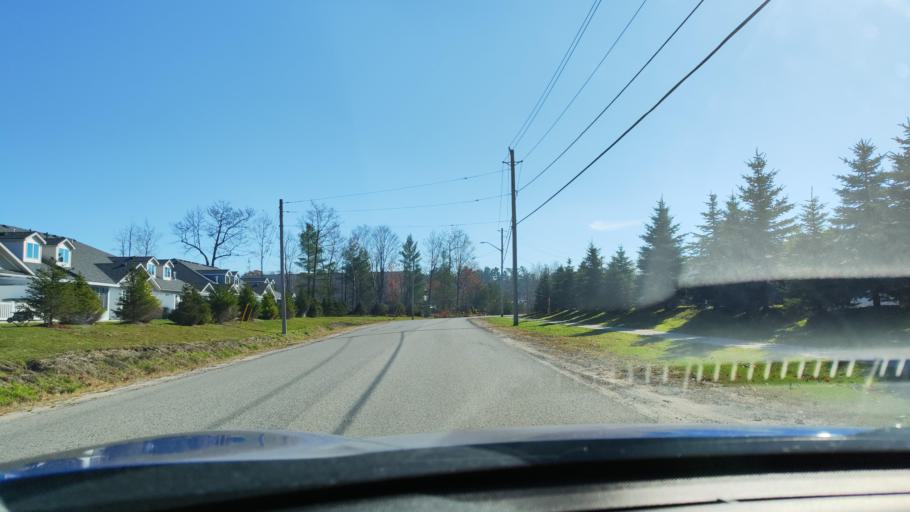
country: CA
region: Ontario
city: Wasaga Beach
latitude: 44.5299
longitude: -79.9982
